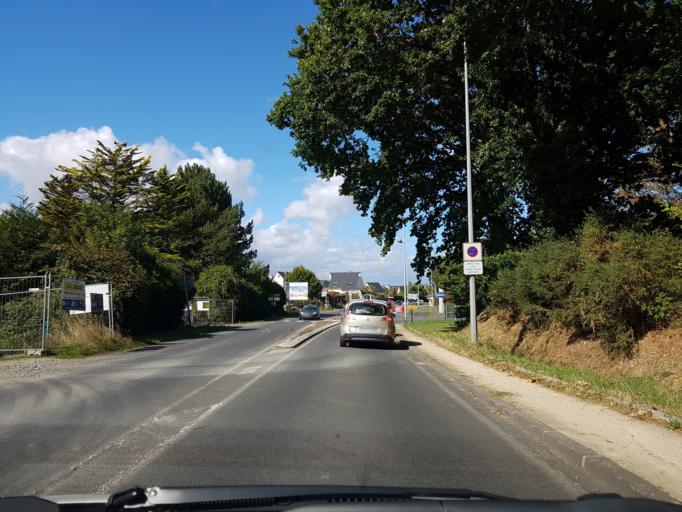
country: FR
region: Brittany
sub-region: Departement des Cotes-d'Armor
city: Saint-Brieuc
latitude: 48.4874
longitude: -2.7519
